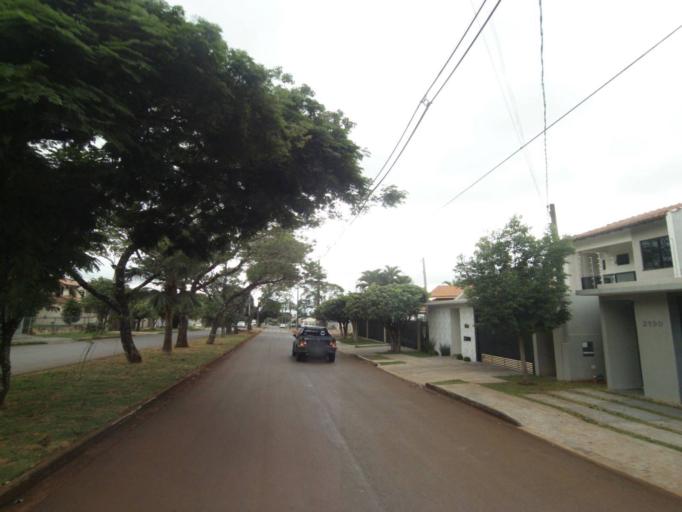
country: BR
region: Parana
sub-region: Campo Mourao
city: Campo Mourao
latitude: -24.0410
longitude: -52.3663
